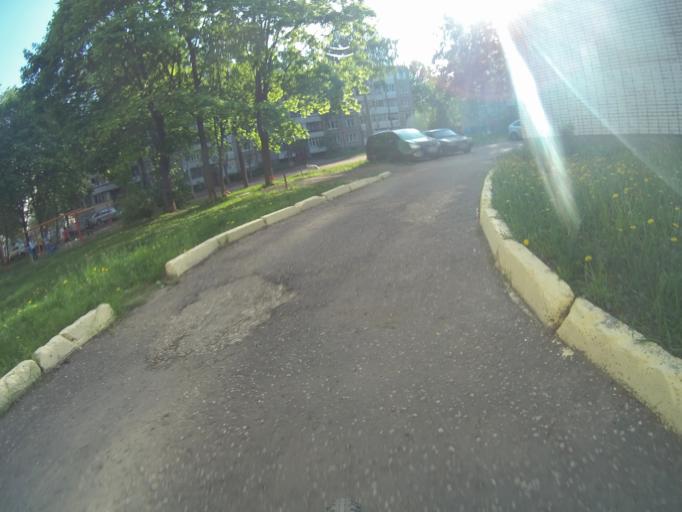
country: RU
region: Vladimir
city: Bogolyubovo
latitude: 56.1653
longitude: 40.4773
